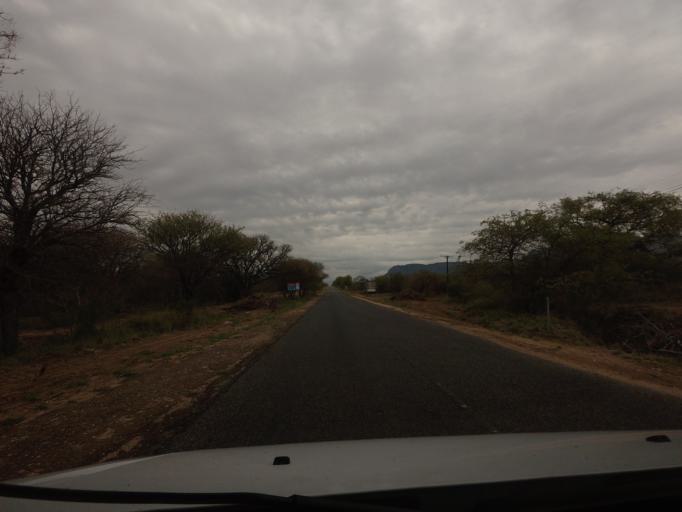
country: ZA
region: Limpopo
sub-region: Mopani District Municipality
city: Hoedspruit
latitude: -24.4733
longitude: 30.8798
